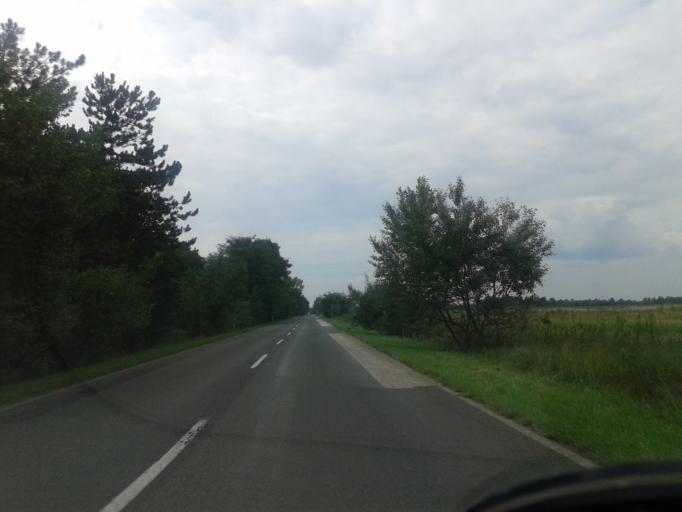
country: HU
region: Csongrad
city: Ruzsa
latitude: 46.2419
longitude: 19.7022
